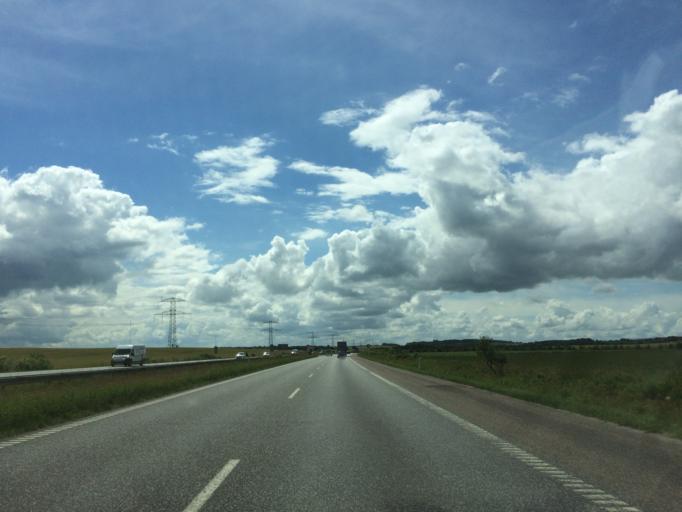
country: DK
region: North Denmark
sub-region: Rebild Kommune
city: Stovring
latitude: 56.8746
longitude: 9.7971
